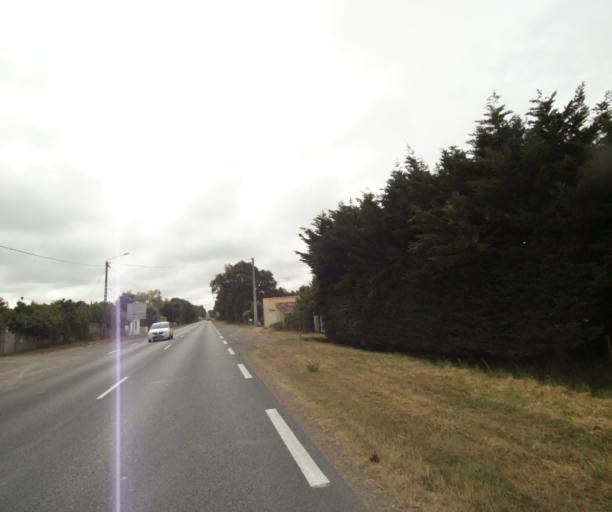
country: FR
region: Pays de la Loire
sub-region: Departement de la Vendee
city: Chateau-d'Olonne
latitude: 46.4809
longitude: -1.7101
